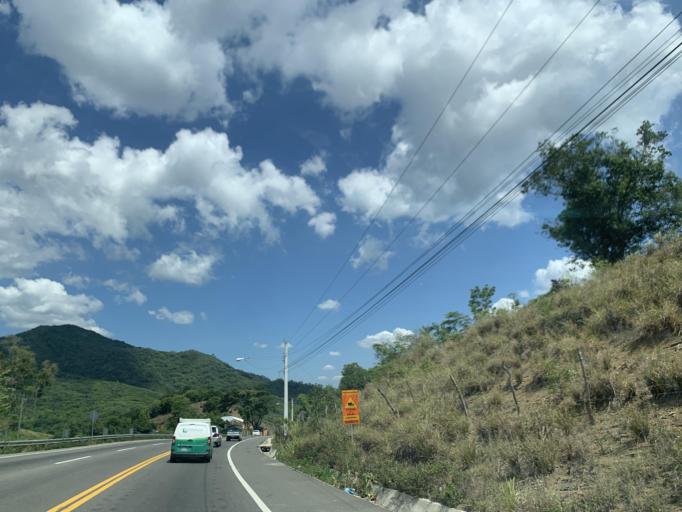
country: DO
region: Puerto Plata
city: Altamira
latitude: 19.6184
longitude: -70.8431
